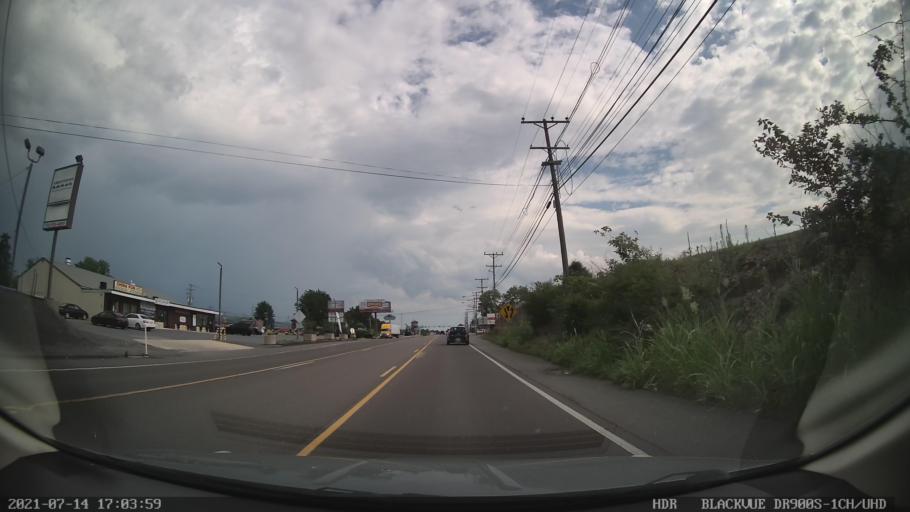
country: US
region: Pennsylvania
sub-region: Berks County
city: Muhlenberg Park
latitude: 40.3874
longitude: -75.9348
